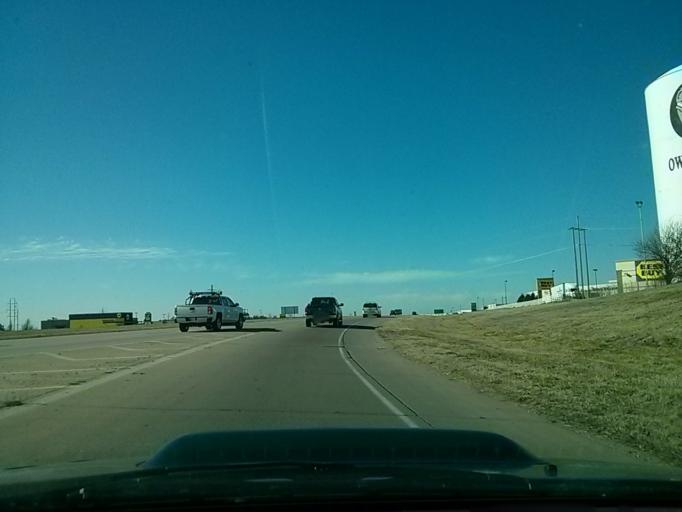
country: US
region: Oklahoma
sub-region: Tulsa County
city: Owasso
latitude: 36.2911
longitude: -95.8377
